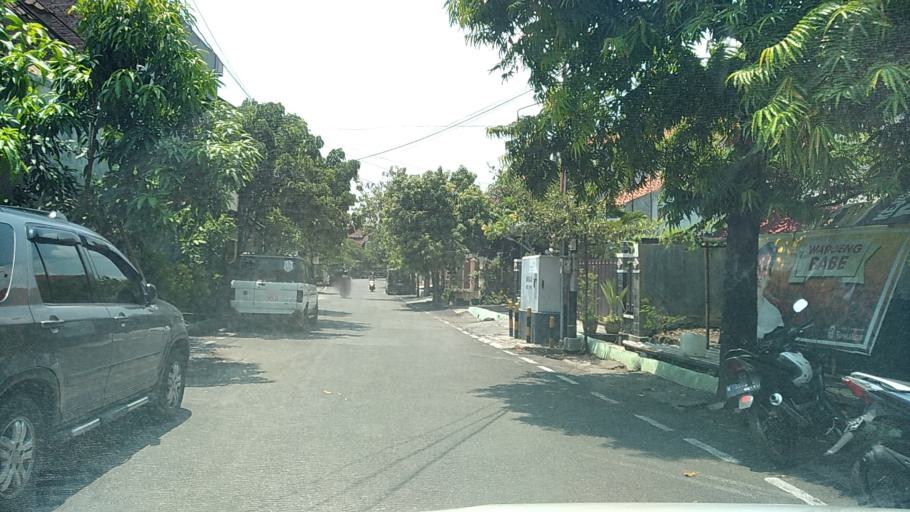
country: ID
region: Central Java
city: Semarang
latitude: -7.0039
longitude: 110.4458
